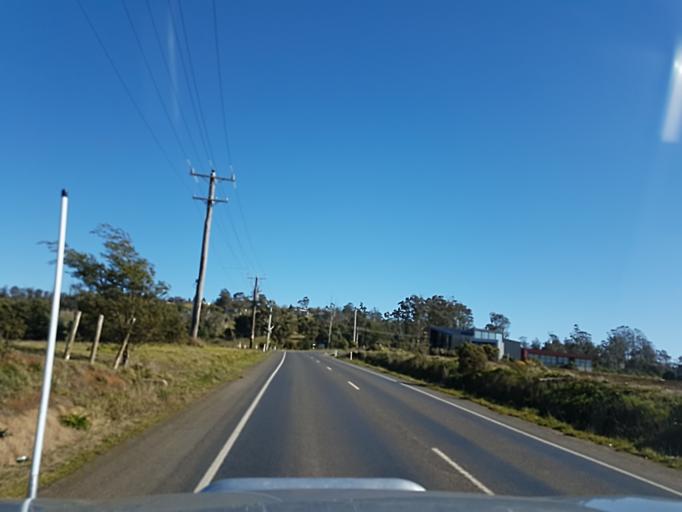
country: AU
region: Victoria
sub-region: Nillumbik
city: Saint Andrews
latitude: -37.5250
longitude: 145.3332
